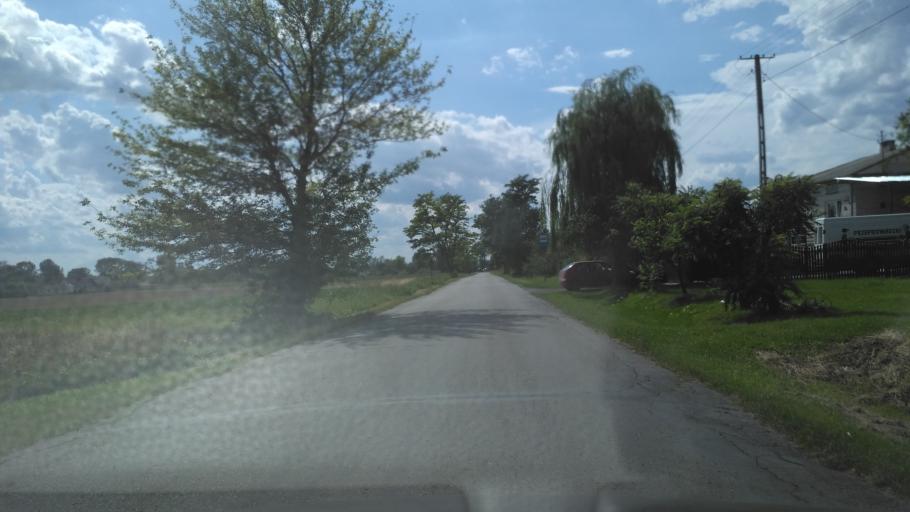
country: PL
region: Lublin Voivodeship
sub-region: Powiat leczynski
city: Milejow
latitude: 51.2174
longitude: 22.8970
